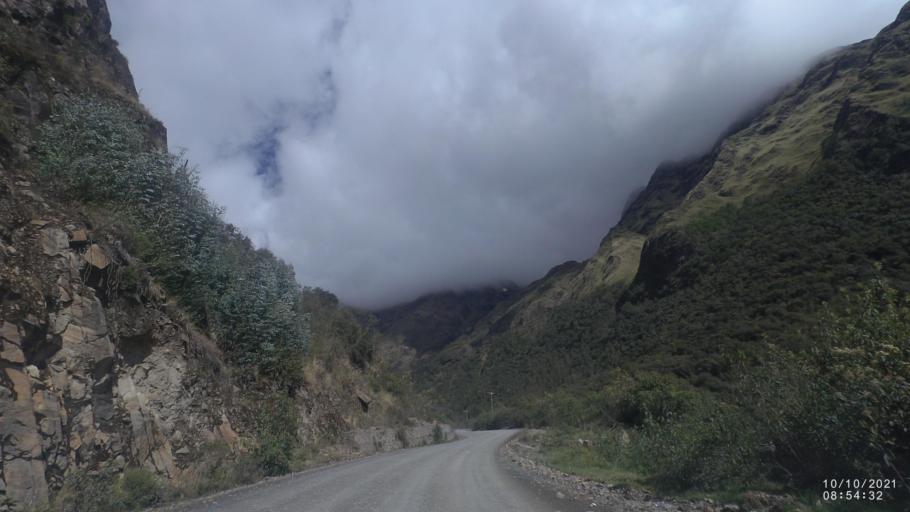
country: BO
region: La Paz
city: Quime
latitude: -16.9886
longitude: -67.2355
